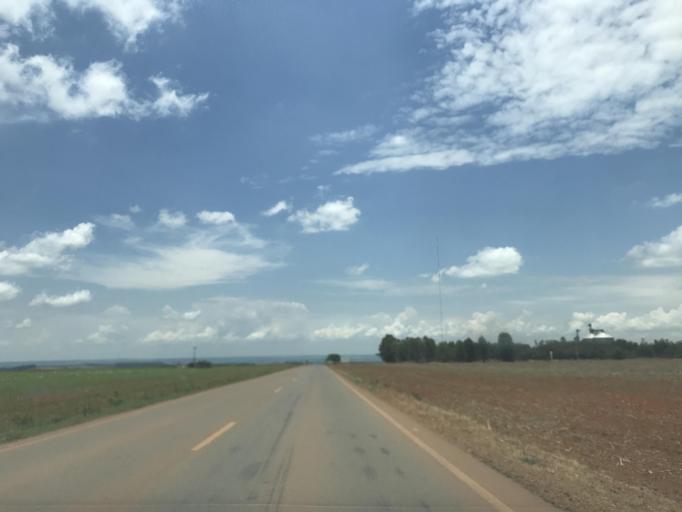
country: BR
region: Goias
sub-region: Vianopolis
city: Vianopolis
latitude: -16.5430
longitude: -48.2610
